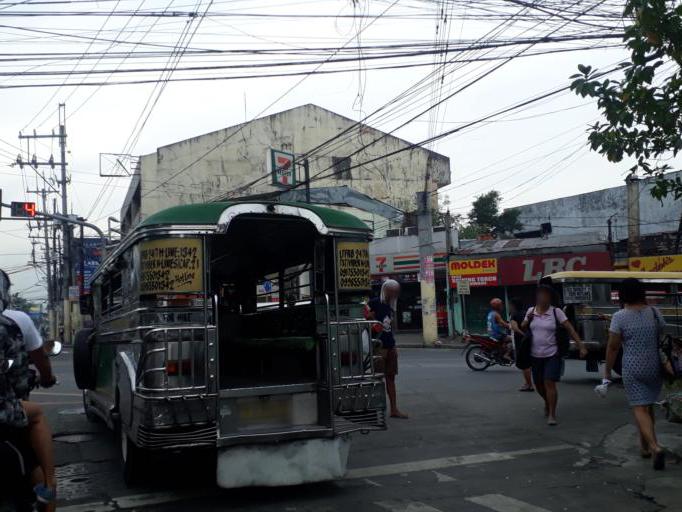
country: PH
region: Metro Manila
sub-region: Caloocan City
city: Niugan
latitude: 14.6583
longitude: 120.9713
